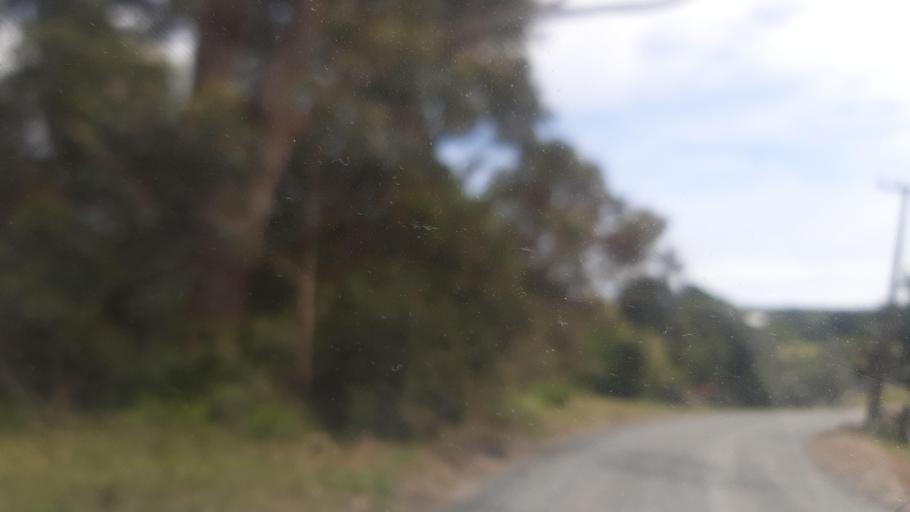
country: NZ
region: Northland
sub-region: Far North District
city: Kaitaia
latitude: -34.8476
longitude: 173.1284
